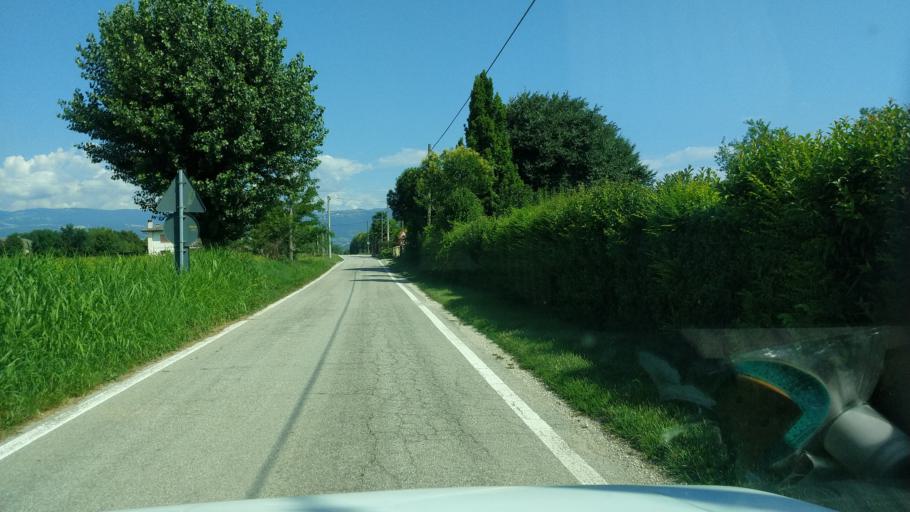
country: IT
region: Veneto
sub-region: Provincia di Vicenza
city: Tezze
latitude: 45.6874
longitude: 11.6806
